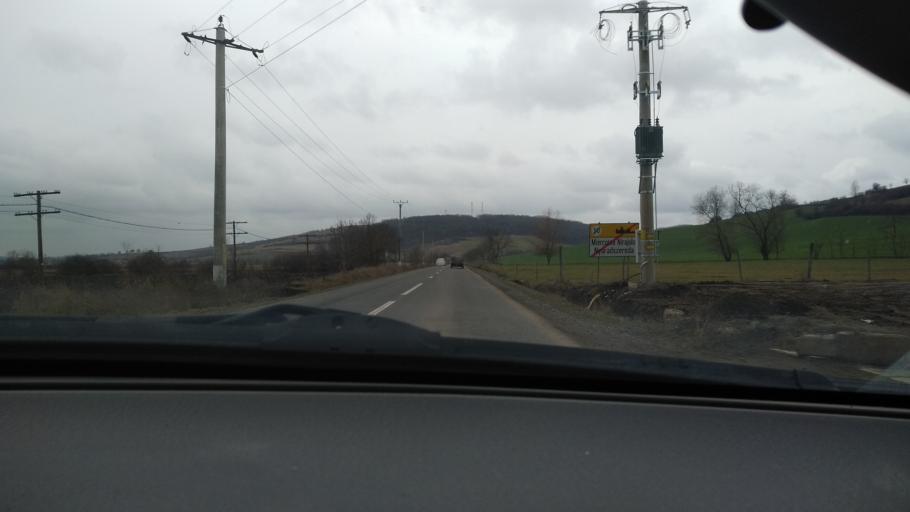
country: RO
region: Mures
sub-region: Comuna Miercurea Nirajului
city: Miercurea Nirajului
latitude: 46.5310
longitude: 24.7845
